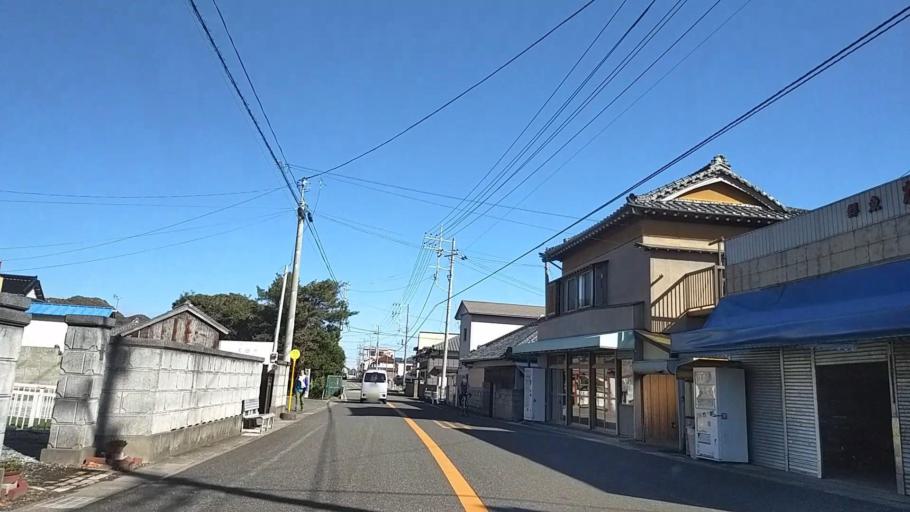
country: JP
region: Chiba
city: Tateyama
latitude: 34.9305
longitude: 139.9459
